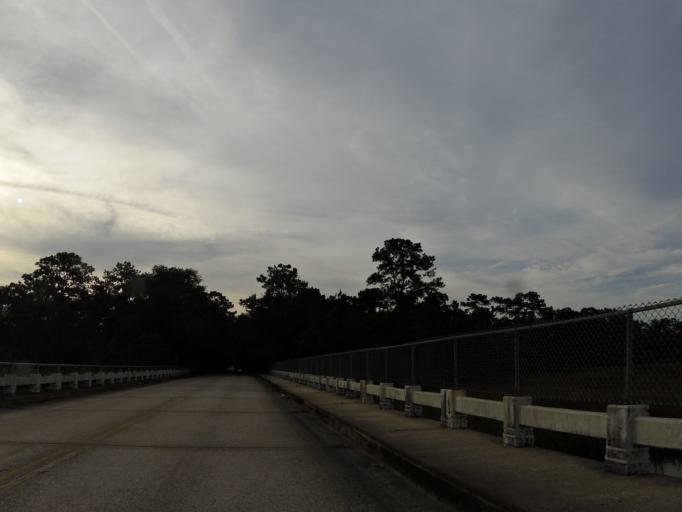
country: US
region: Florida
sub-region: Duval County
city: Jacksonville
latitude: 30.3937
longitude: -81.7133
